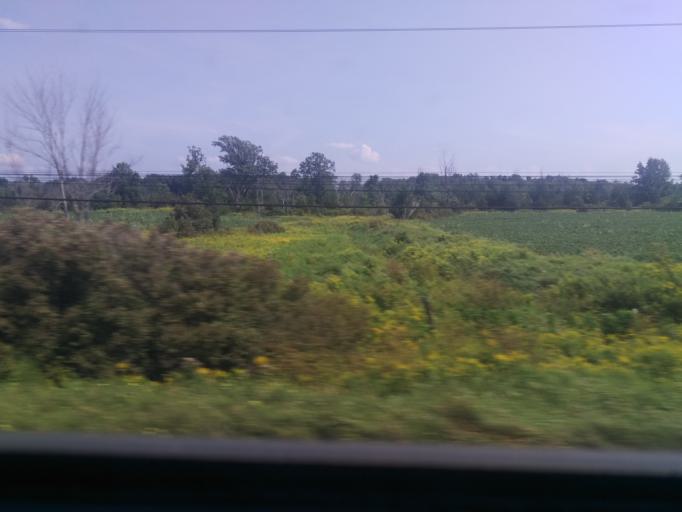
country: US
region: New York
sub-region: Jefferson County
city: Alexandria Bay
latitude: 44.4724
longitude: -75.8938
